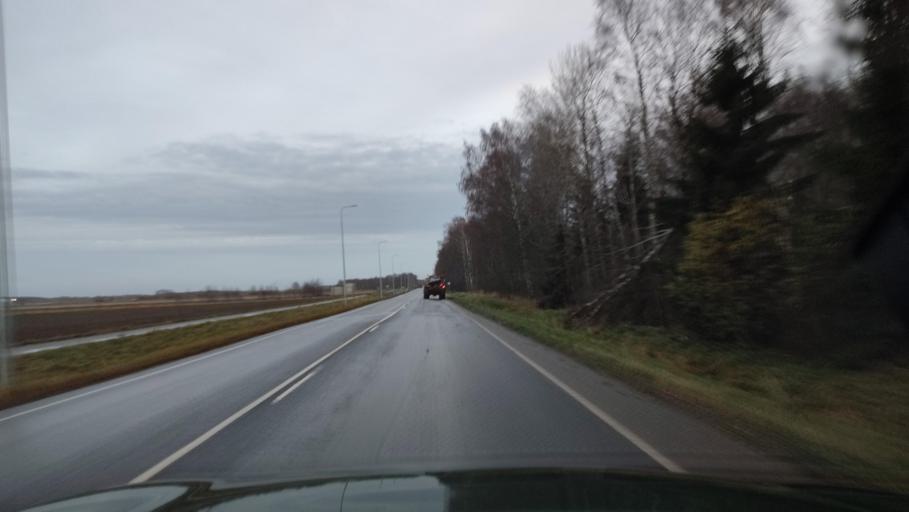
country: FI
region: Ostrobothnia
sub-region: Vaasa
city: Ristinummi
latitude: 63.0471
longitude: 21.7310
